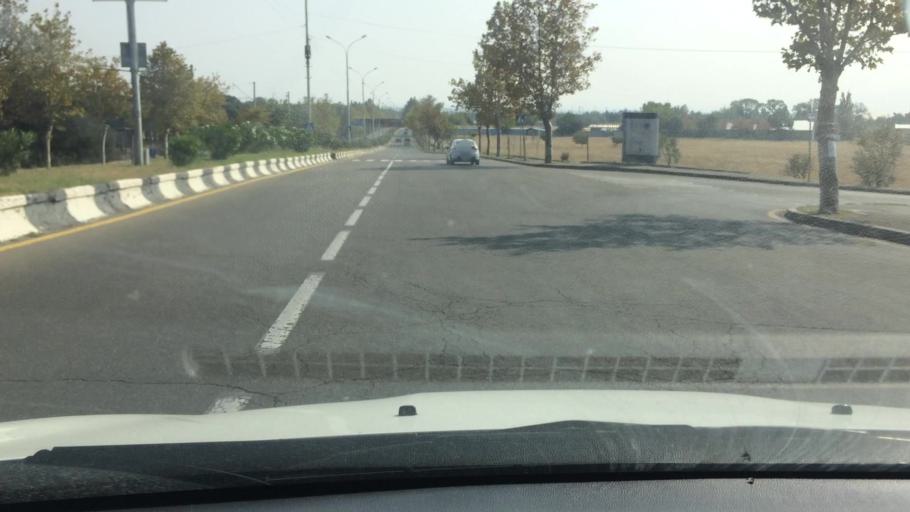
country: GE
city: Didi Lilo
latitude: 41.6834
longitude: 44.9547
